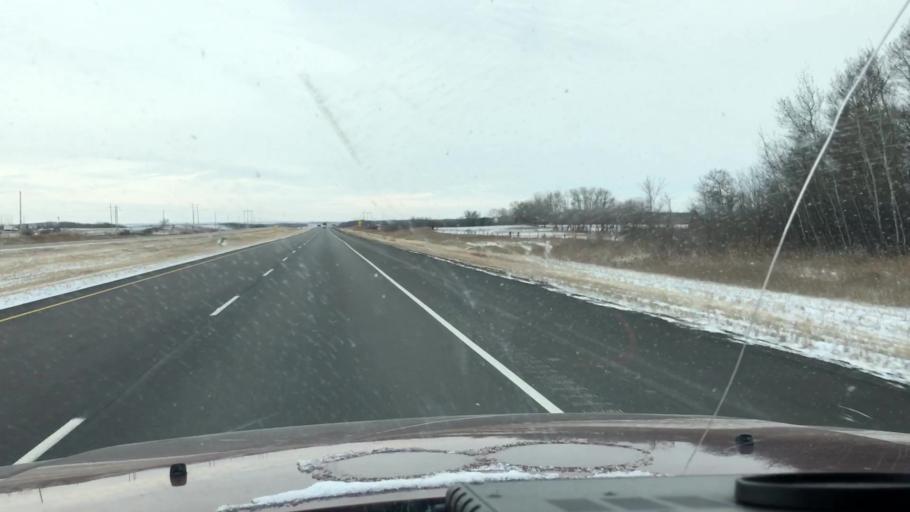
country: CA
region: Saskatchewan
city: Saskatoon
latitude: 51.8991
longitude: -106.5209
